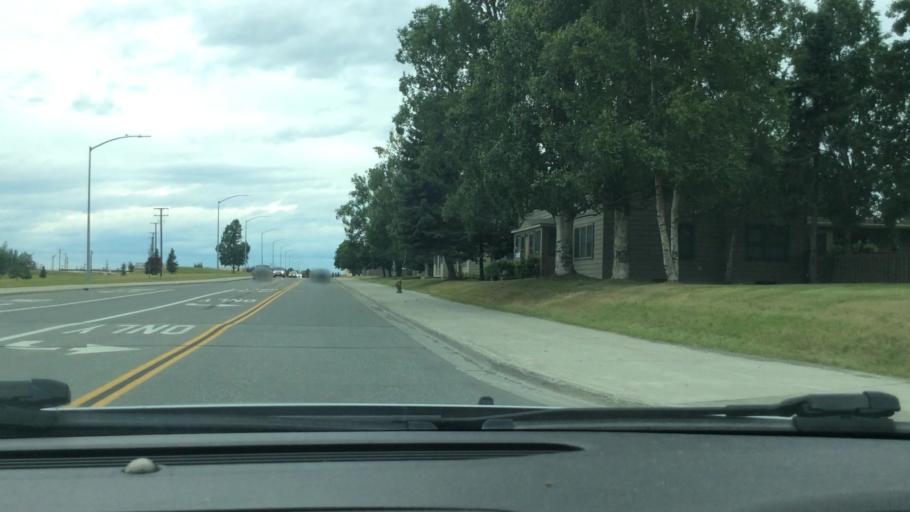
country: US
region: Alaska
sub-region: Anchorage Municipality
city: Anchorage
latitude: 61.2383
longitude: -149.8169
